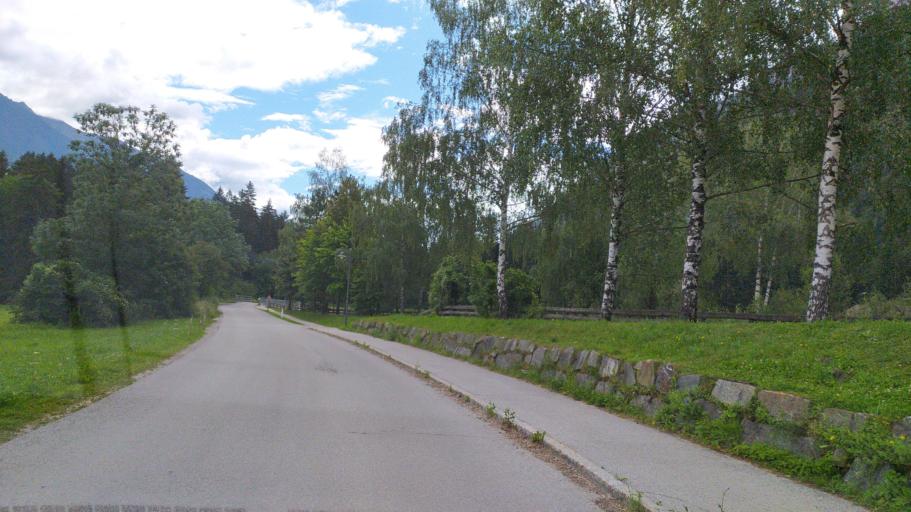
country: AT
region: Tyrol
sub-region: Politischer Bezirk Lienz
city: Lavant
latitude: 46.7967
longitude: 12.8471
